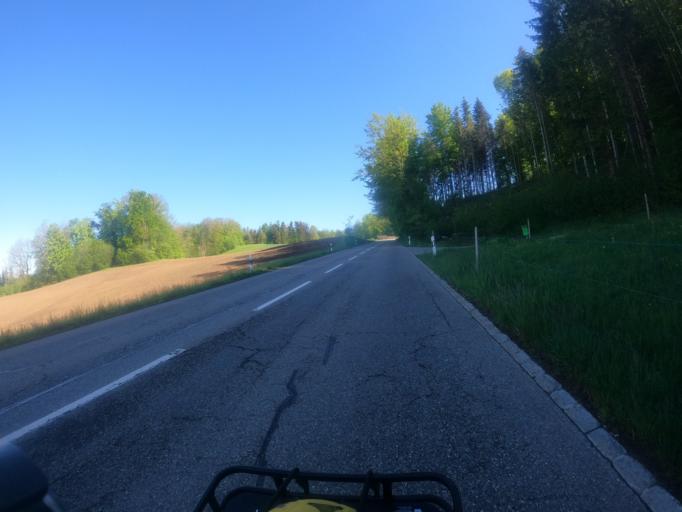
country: CH
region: Zurich
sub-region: Bezirk Affoltern
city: Affoltern / Sonnenberg
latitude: 47.2795
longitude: 8.4701
